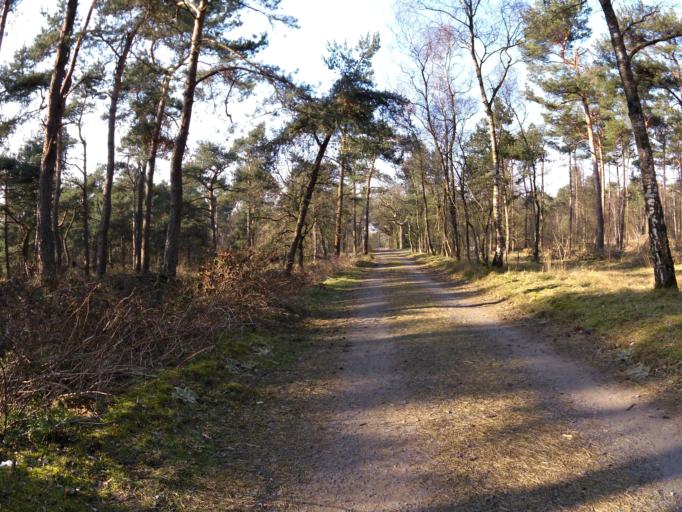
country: NL
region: North Brabant
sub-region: Gemeente Maasdonk
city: Geffen
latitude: 51.7194
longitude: 5.4114
